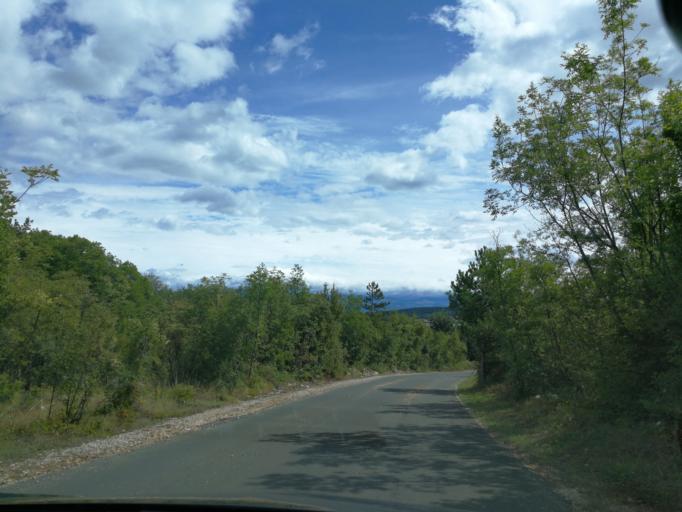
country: HR
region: Primorsko-Goranska
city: Omisalj
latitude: 45.1669
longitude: 14.5983
